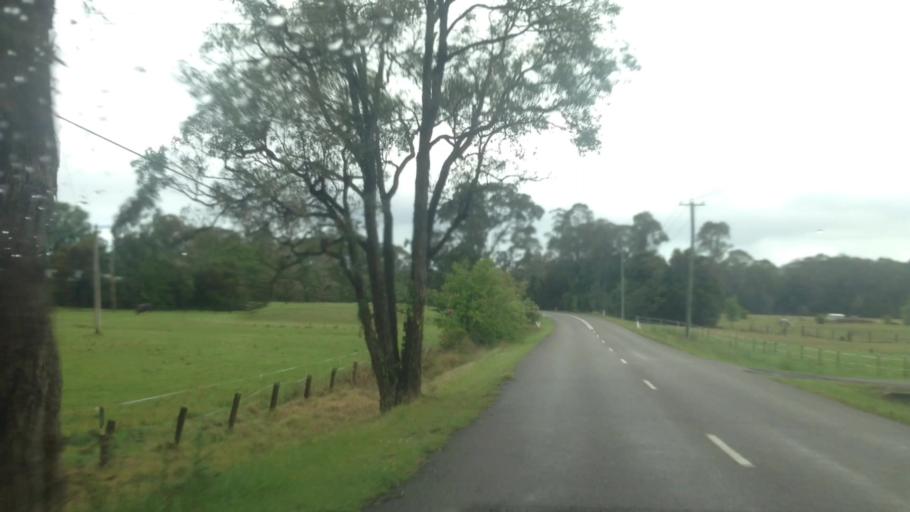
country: AU
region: New South Wales
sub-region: Wyong Shire
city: Little Jilliby
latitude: -33.2502
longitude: 151.3833
